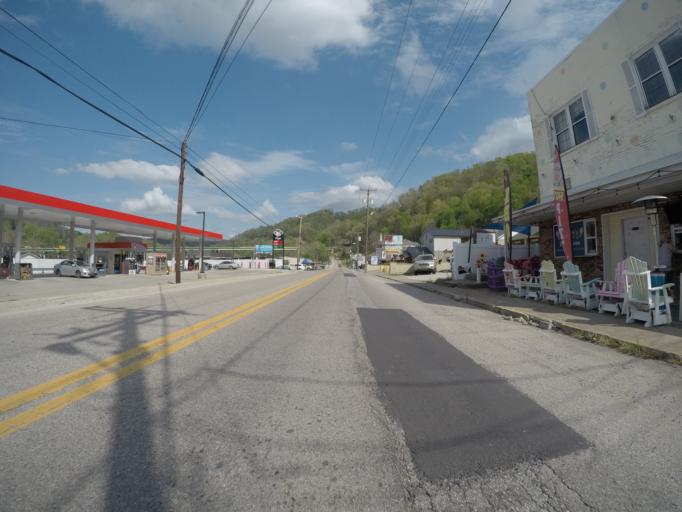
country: US
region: West Virginia
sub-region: Boone County
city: Madison
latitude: 38.0822
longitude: -81.8350
